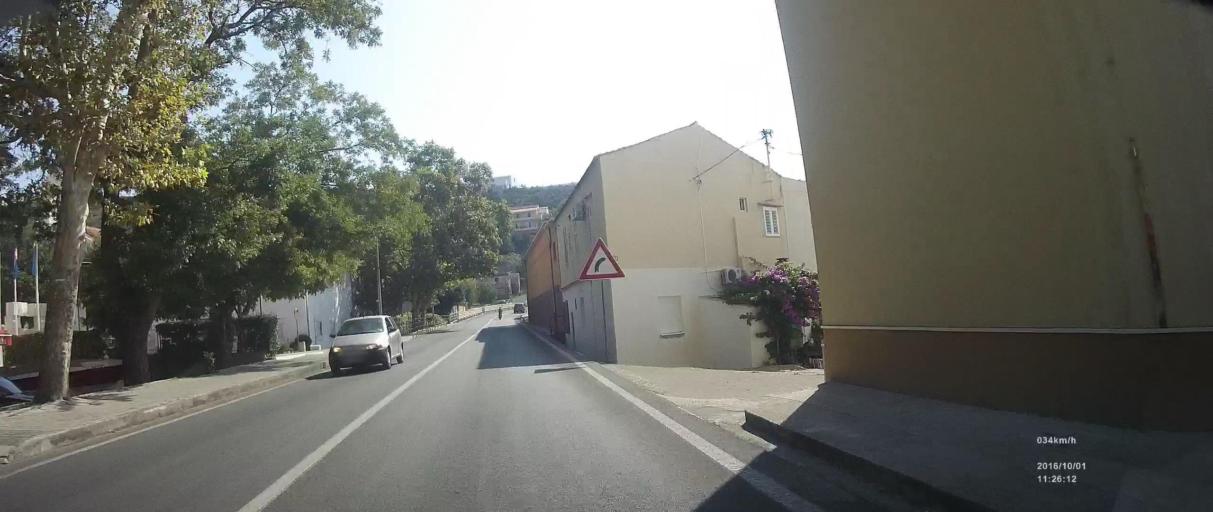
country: HR
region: Splitsko-Dalmatinska
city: Duce
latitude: 43.4437
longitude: 16.6419
